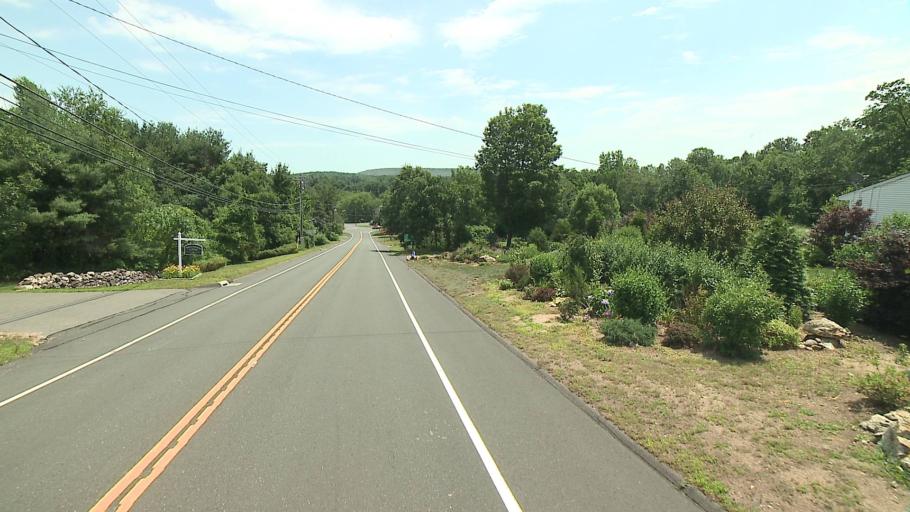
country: US
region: Connecticut
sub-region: Hartford County
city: North Granby
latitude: 41.9958
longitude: -72.8332
